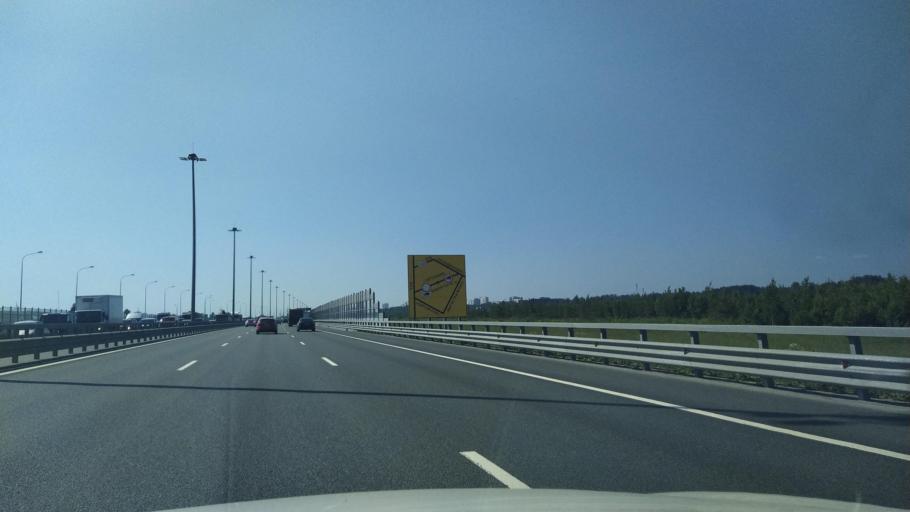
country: RU
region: St.-Petersburg
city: Pargolovo
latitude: 60.0962
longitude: 30.3138
